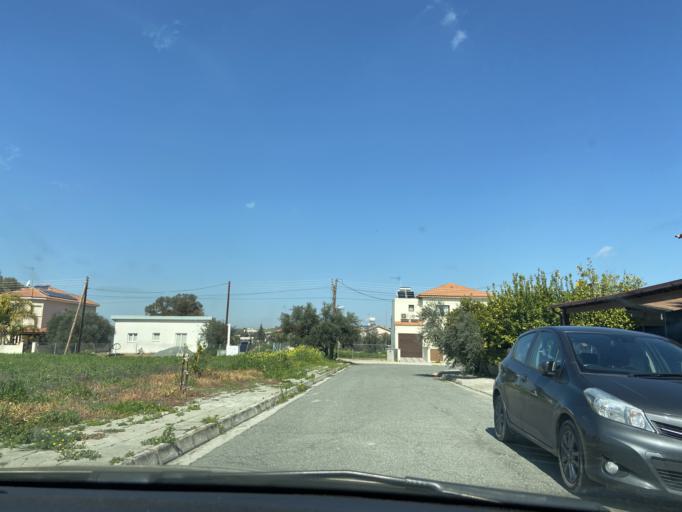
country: CY
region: Lefkosia
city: Dali
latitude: 35.0168
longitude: 33.3990
